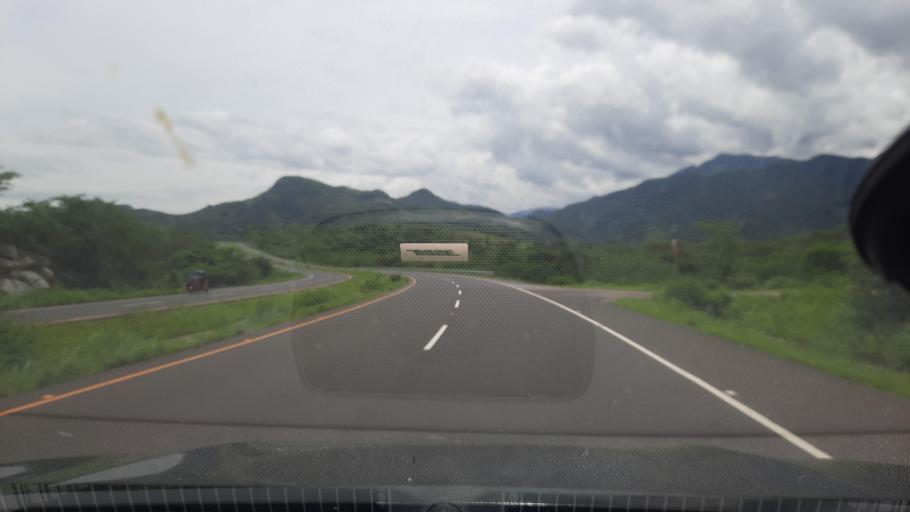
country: HN
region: Valle
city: Aramecina
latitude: 13.7740
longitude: -87.7002
